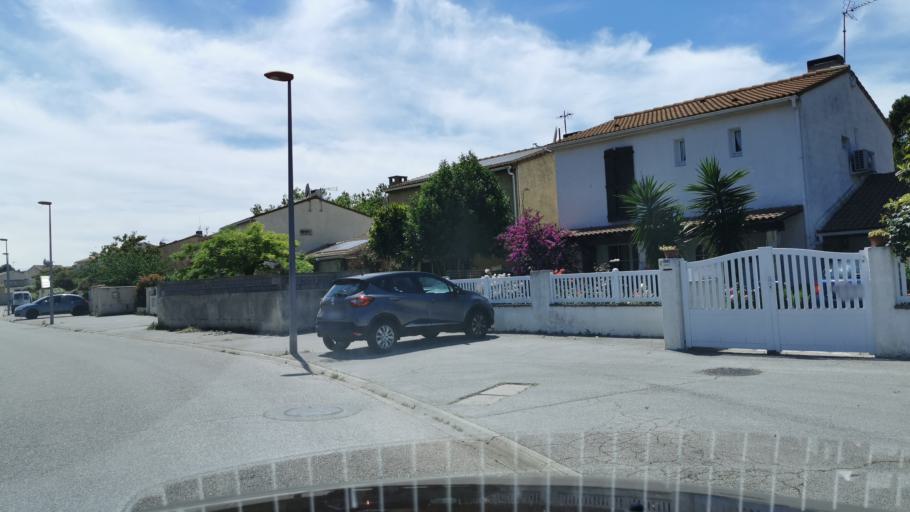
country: FR
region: Languedoc-Roussillon
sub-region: Departement de l'Aude
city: Narbonne
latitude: 43.1882
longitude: 2.9844
